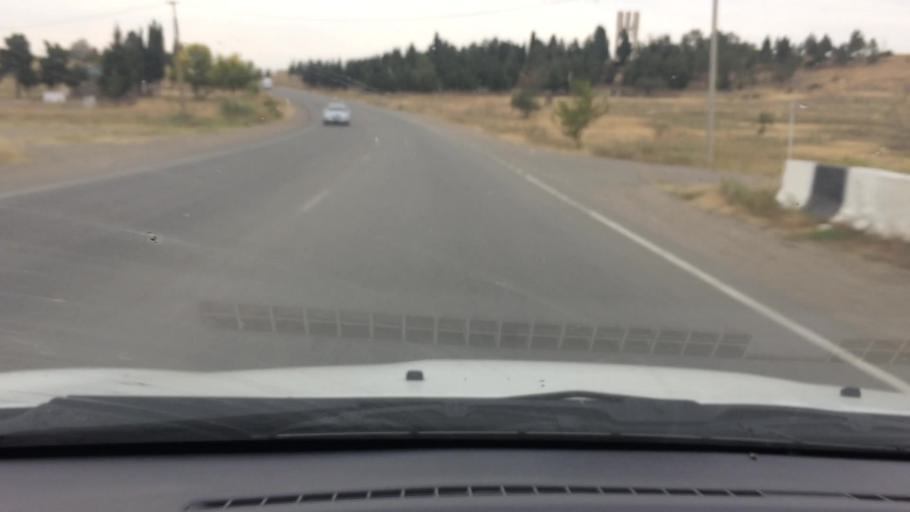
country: GE
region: Kvemo Kartli
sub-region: Marneuli
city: Marneuli
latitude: 41.5267
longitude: 44.7770
